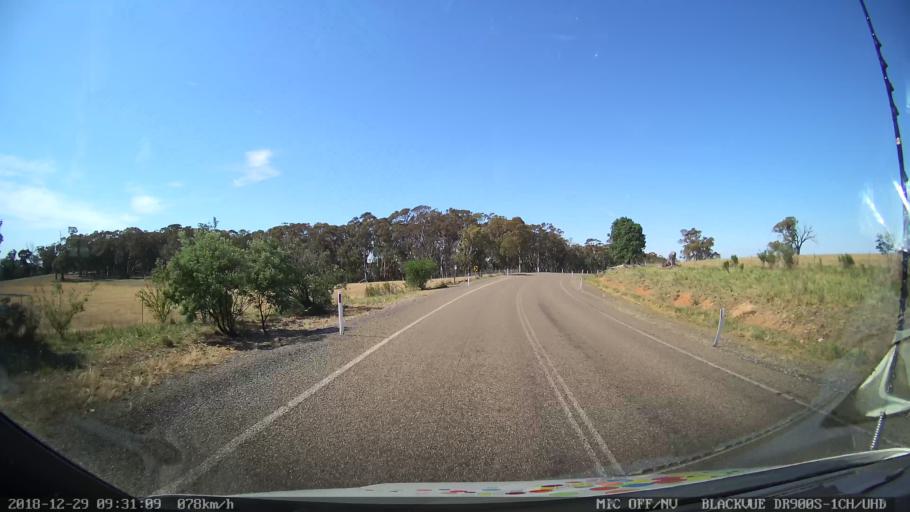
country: AU
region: New South Wales
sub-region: Upper Lachlan Shire
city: Crookwell
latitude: -34.6051
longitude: 149.3652
